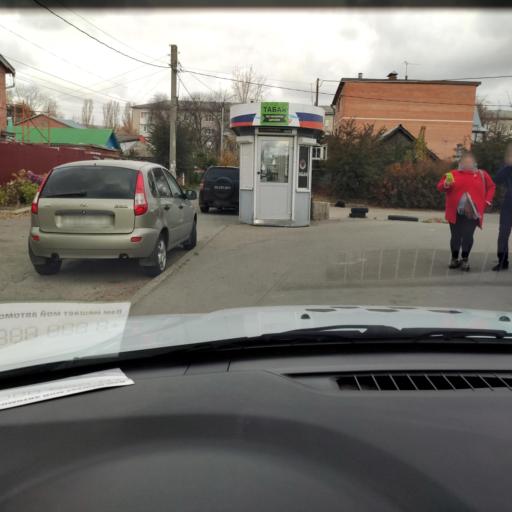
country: RU
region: Samara
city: Tol'yatti
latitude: 53.5194
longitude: 49.4104
